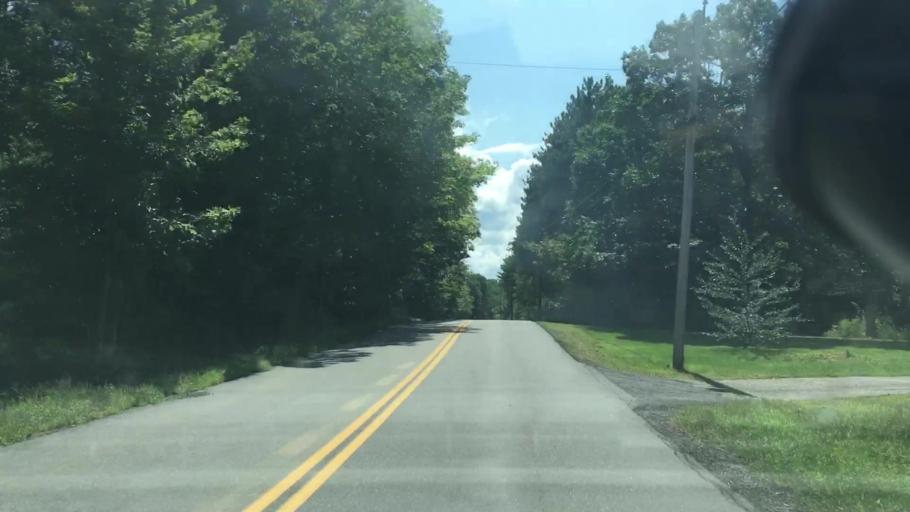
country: US
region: Maine
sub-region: Somerset County
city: Skowhegan
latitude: 44.6993
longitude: -69.6946
